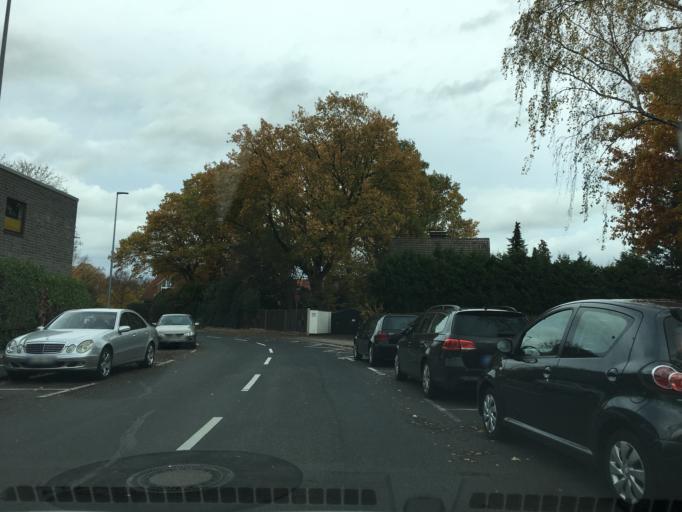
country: DE
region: North Rhine-Westphalia
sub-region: Regierungsbezirk Dusseldorf
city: Kaarst
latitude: 51.2284
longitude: 6.6001
